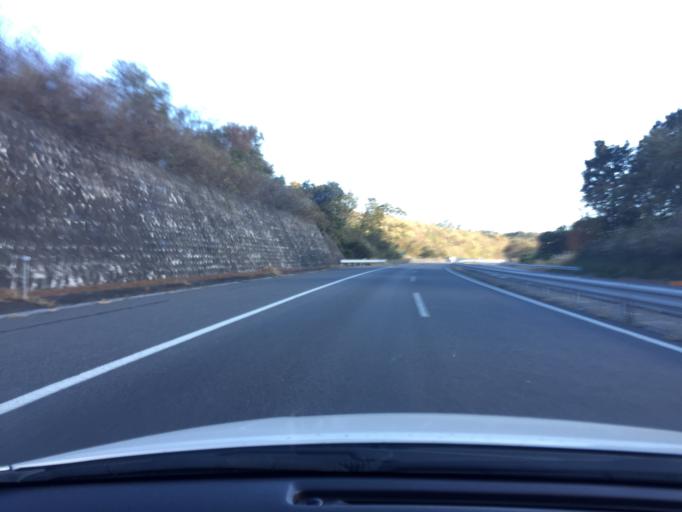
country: JP
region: Fukushima
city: Ishikawa
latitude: 37.2207
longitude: 140.6894
